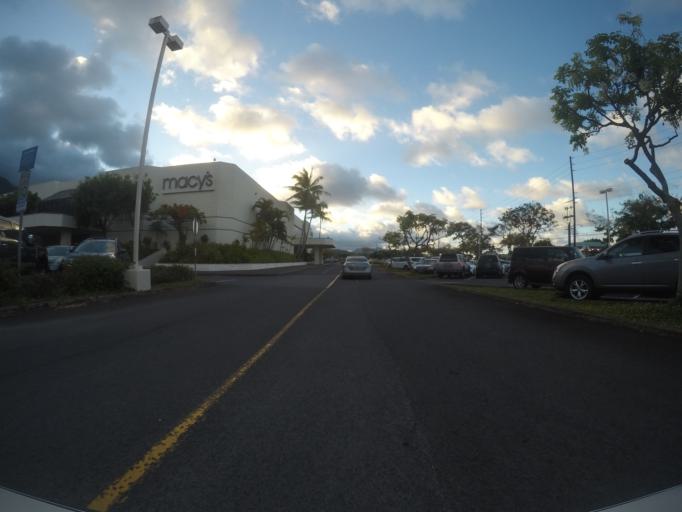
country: US
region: Hawaii
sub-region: Honolulu County
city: He'eia
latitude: 21.4201
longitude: -157.8036
